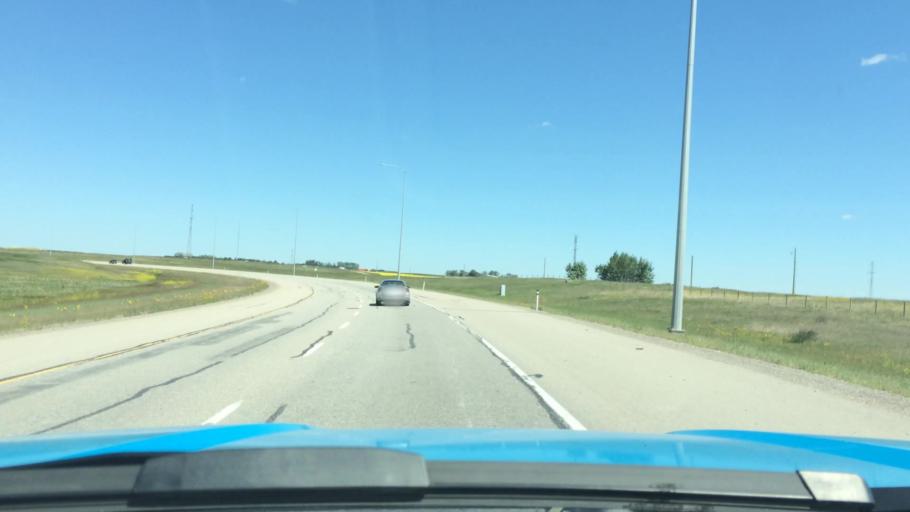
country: CA
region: Alberta
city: Chestermere
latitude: 51.1710
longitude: -113.9133
